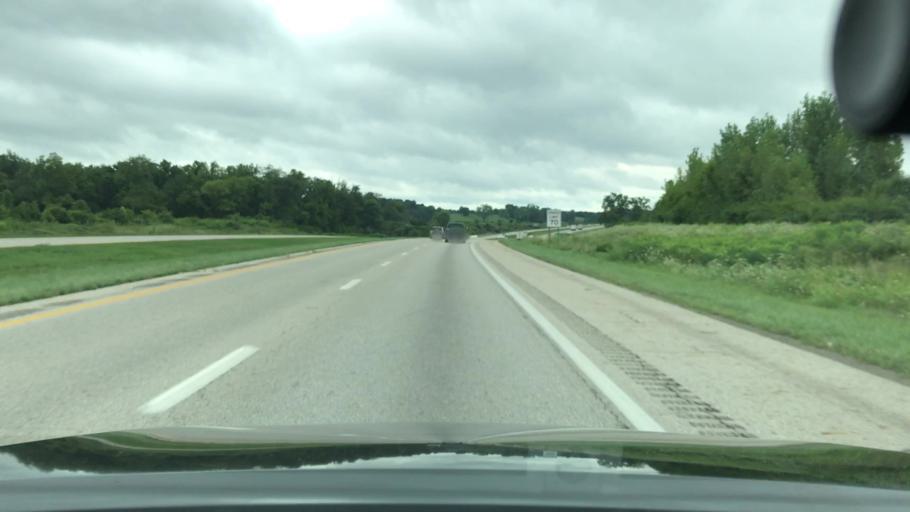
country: US
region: Ohio
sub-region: Ross County
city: Chillicothe
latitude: 39.2930
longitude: -82.9002
